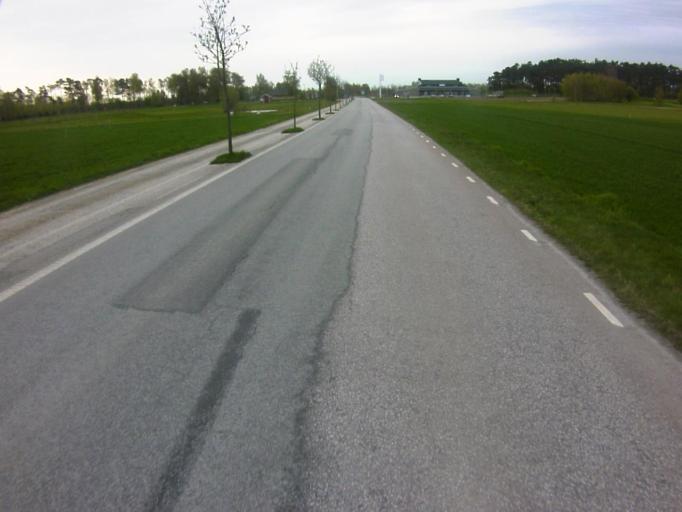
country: SE
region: Skane
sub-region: Kavlinge Kommun
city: Loddekopinge
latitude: 55.7707
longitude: 13.0114
